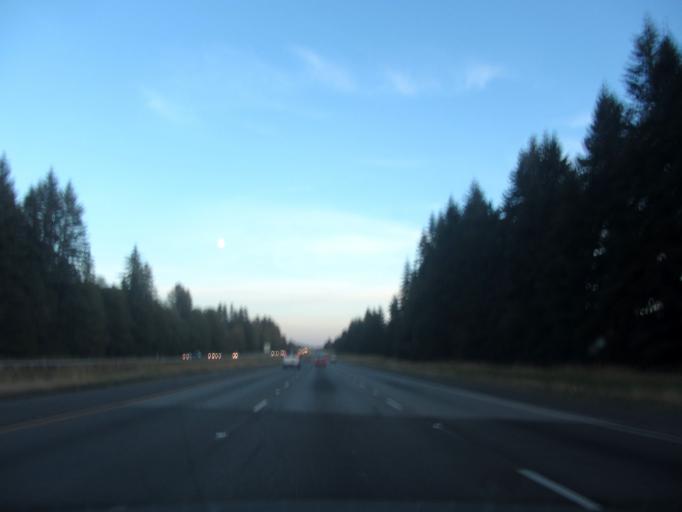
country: US
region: Washington
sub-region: Snohomish County
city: Stanwood
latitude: 48.2869
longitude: -122.2915
